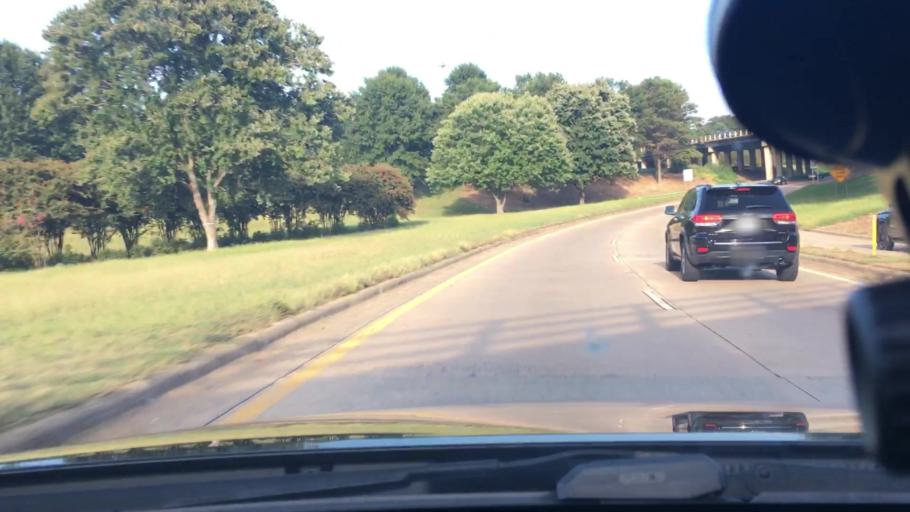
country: US
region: North Carolina
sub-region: Mecklenburg County
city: Charlotte
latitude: 35.2210
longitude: -80.8293
